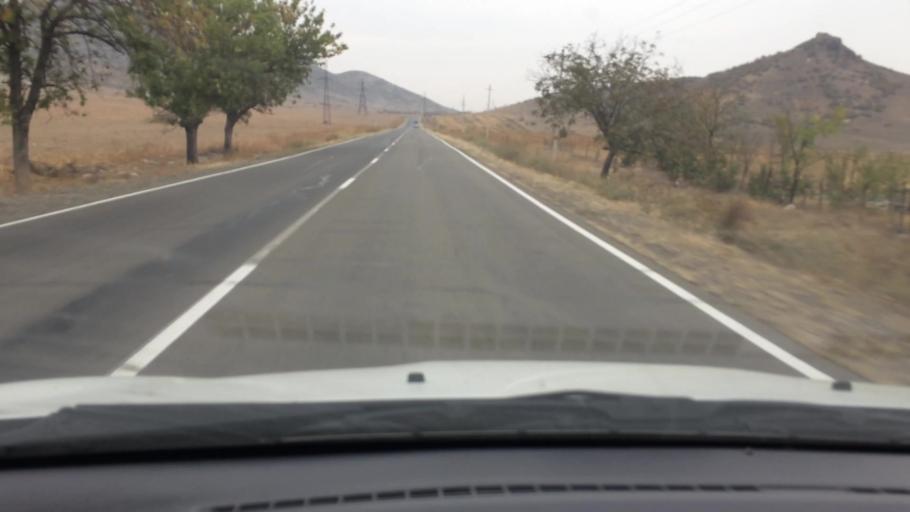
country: GE
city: Naghvarevi
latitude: 41.3478
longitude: 44.8173
